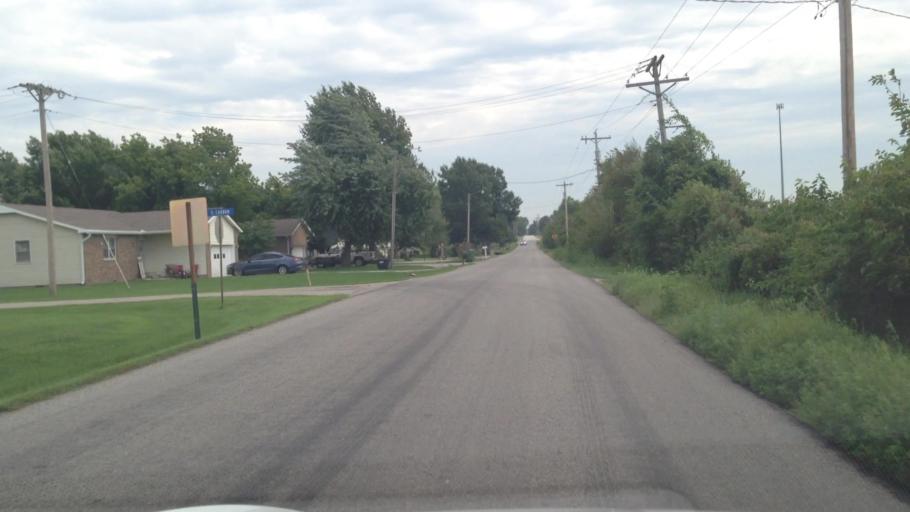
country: US
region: Kansas
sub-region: Crawford County
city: Girard
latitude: 37.4992
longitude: -94.8476
